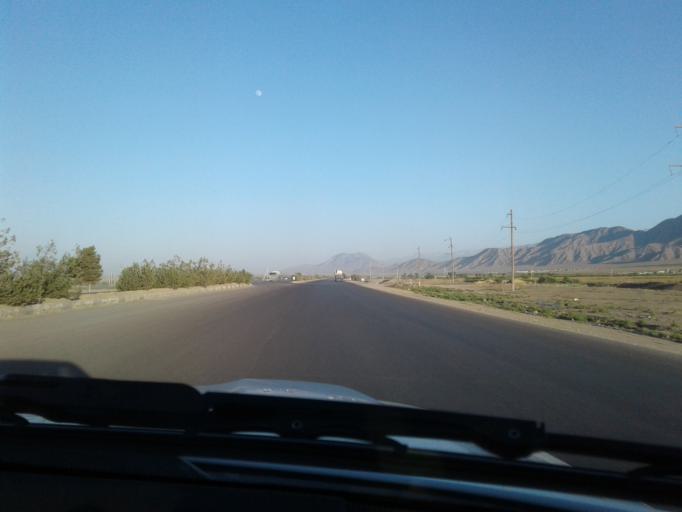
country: TM
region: Ahal
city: Baharly
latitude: 38.2252
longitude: 57.7949
